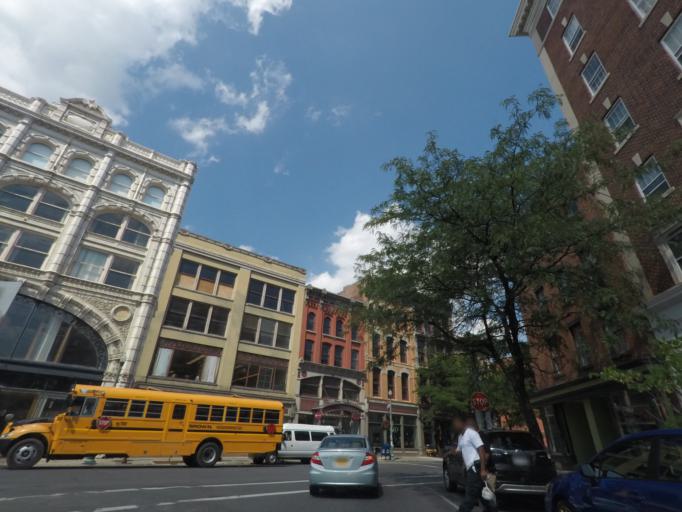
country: US
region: New York
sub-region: Rensselaer County
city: Troy
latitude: 42.7316
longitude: -73.6915
